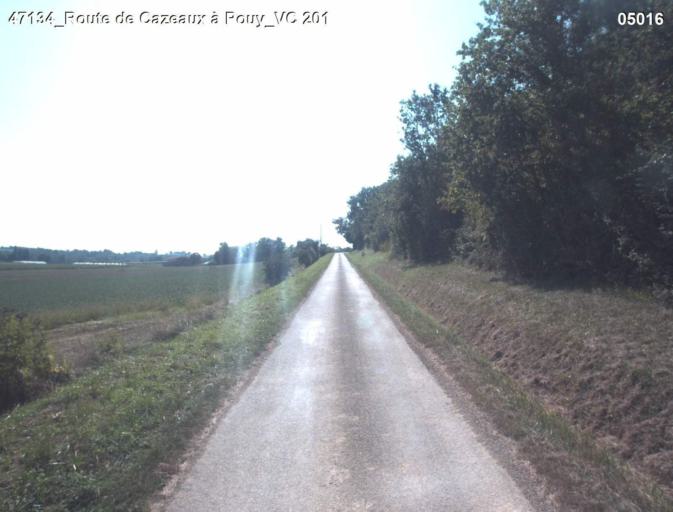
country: FR
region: Aquitaine
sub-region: Departement du Lot-et-Garonne
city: Mezin
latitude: 44.0406
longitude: 0.3117
